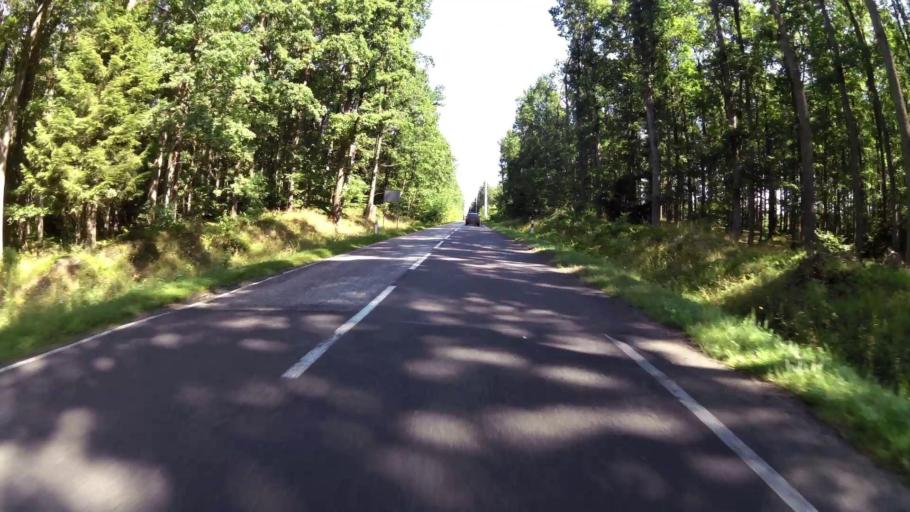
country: PL
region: West Pomeranian Voivodeship
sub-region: Powiat drawski
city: Czaplinek
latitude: 53.4468
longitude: 16.2119
